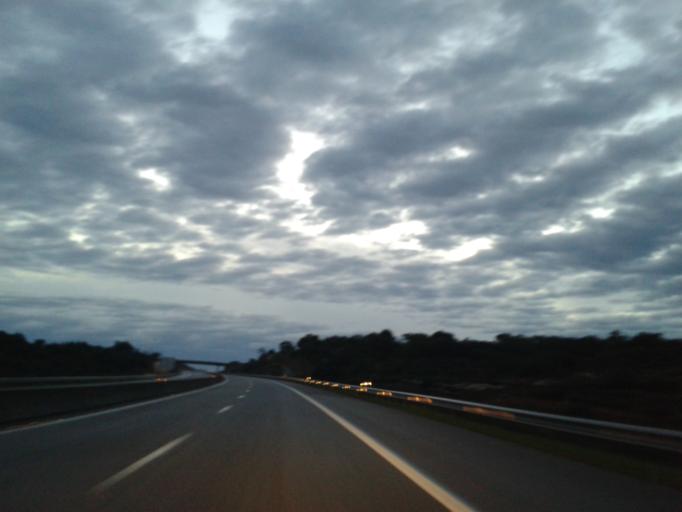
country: PT
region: Faro
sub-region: Portimao
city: Alvor
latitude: 37.1769
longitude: -8.6212
